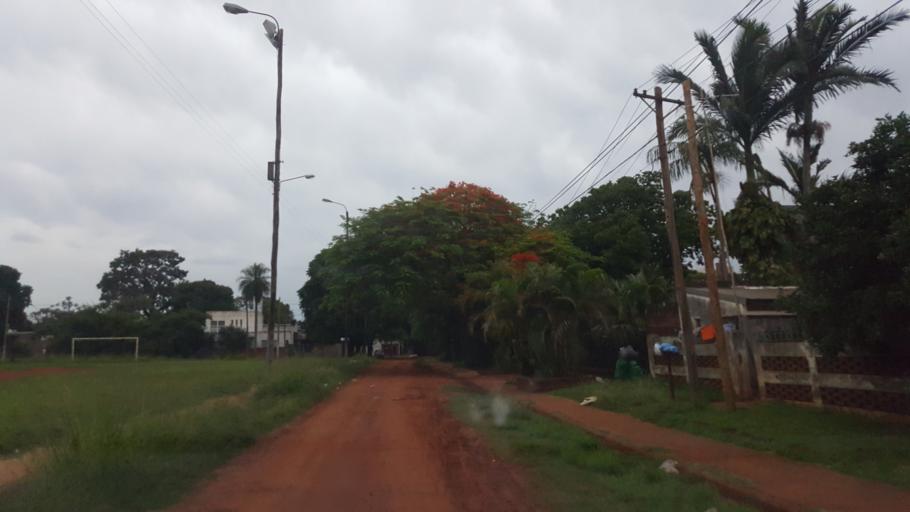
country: AR
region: Misiones
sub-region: Departamento de Capital
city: Posadas
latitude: -27.3699
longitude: -55.9272
